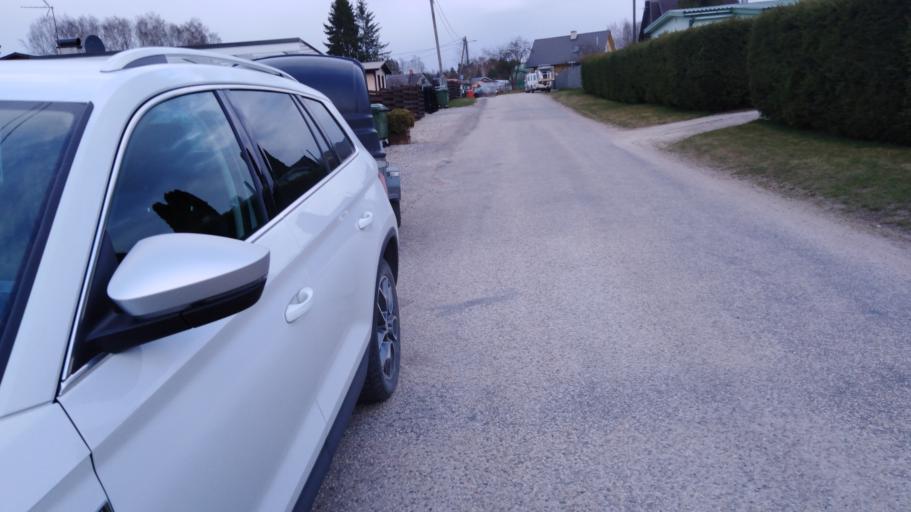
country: EE
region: Vorumaa
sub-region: Voru linn
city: Voru
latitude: 57.8073
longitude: 27.0153
